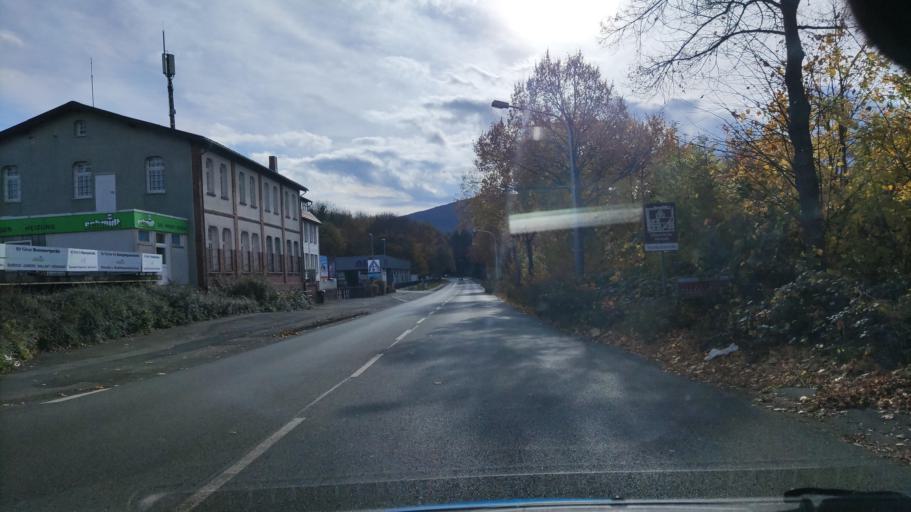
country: DE
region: Lower Saxony
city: Goslar
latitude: 51.9178
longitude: 10.4164
